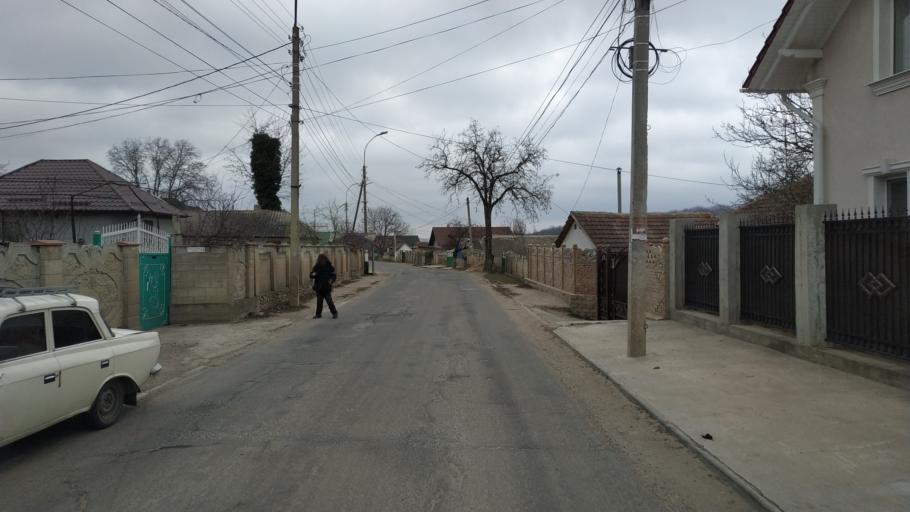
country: MD
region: Laloveni
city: Ialoveni
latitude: 46.9038
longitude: 28.8072
